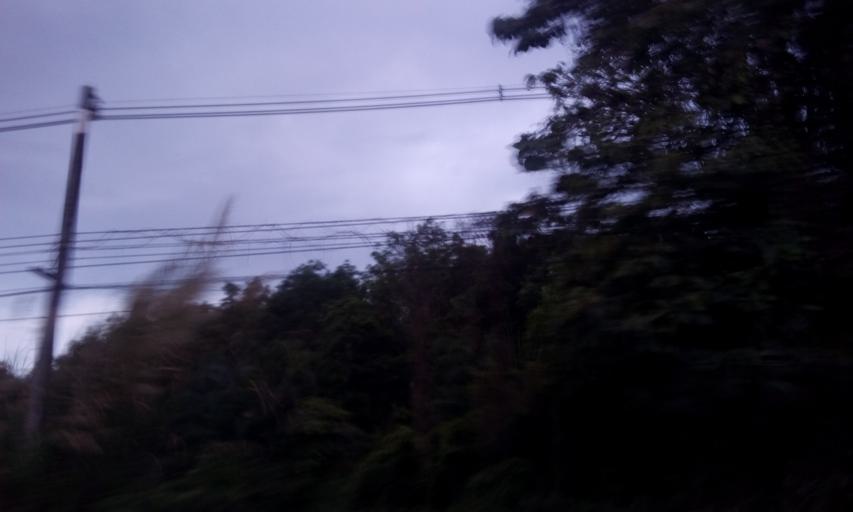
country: TH
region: Chanthaburi
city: Khlung
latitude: 12.4497
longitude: 102.2861
